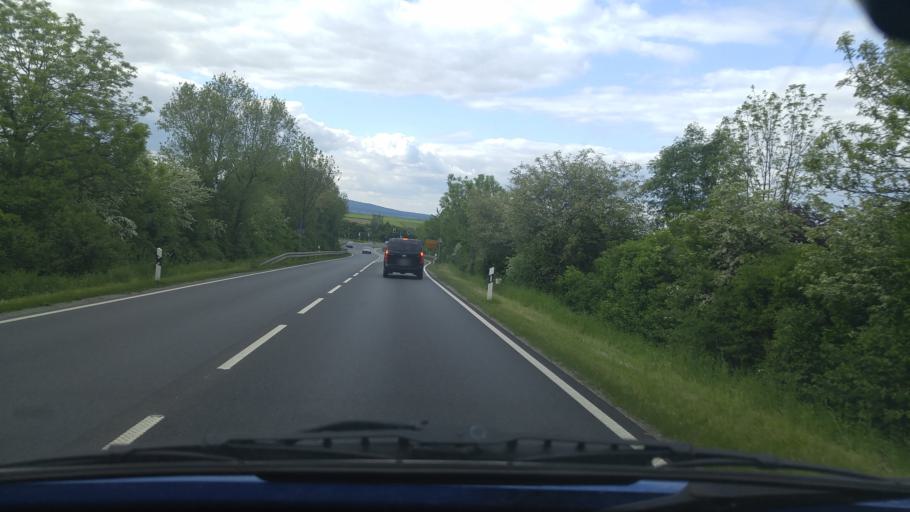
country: DE
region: Hesse
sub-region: Regierungsbezirk Darmstadt
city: Karben
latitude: 50.2285
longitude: 8.7350
